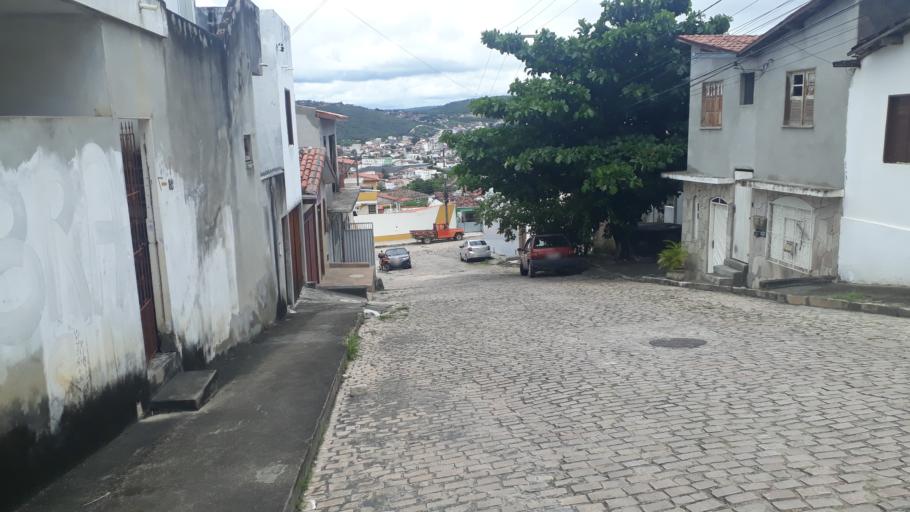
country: BR
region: Bahia
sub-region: Jacobina
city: Jacobina
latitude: -11.1928
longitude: -40.5161
